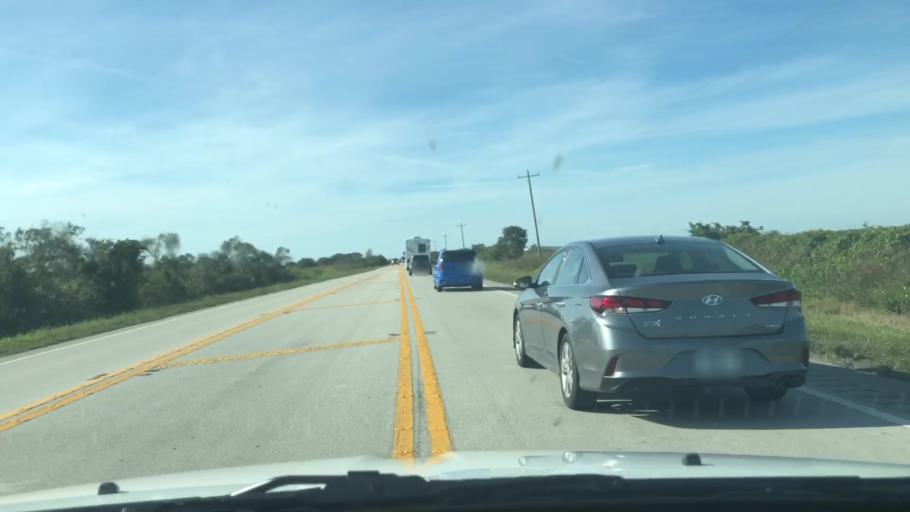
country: US
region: Florida
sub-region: Polk County
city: Babson Park
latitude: 27.7866
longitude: -81.1443
